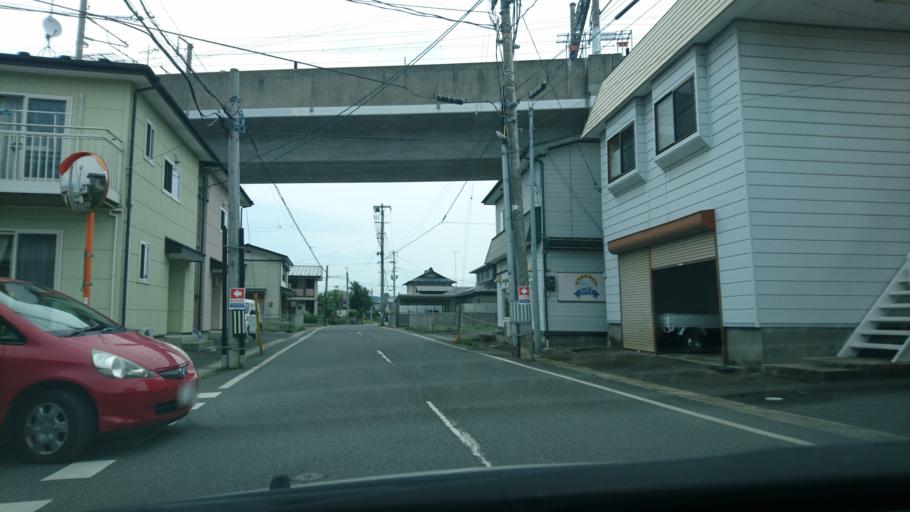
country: JP
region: Iwate
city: Ichinoseki
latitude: 38.9328
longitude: 141.1415
